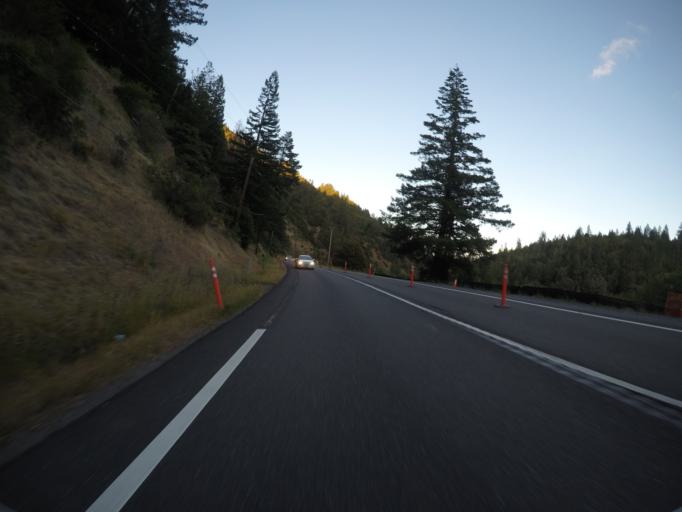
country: US
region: California
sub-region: Humboldt County
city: Redway
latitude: 39.8919
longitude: -123.7528
